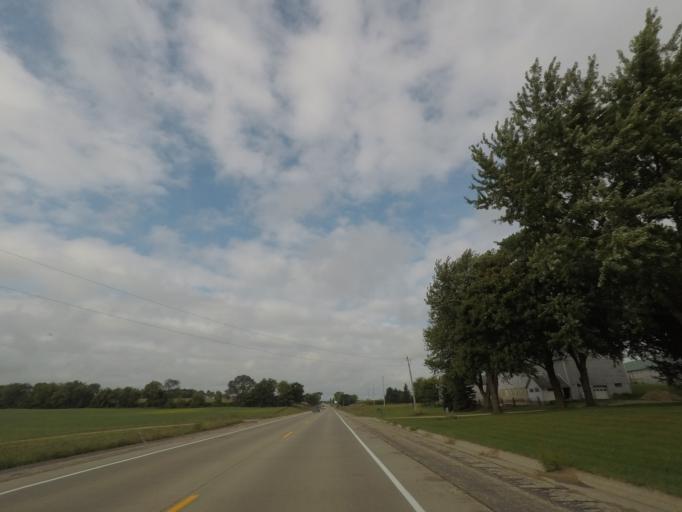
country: US
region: Wisconsin
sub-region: Dane County
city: Deerfield
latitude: 43.0318
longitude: -89.1425
